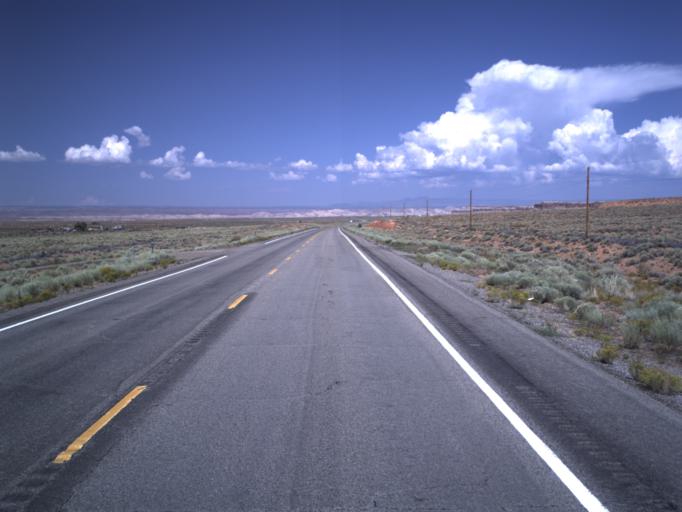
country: US
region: Utah
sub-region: San Juan County
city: Blanding
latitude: 37.1468
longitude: -109.5632
